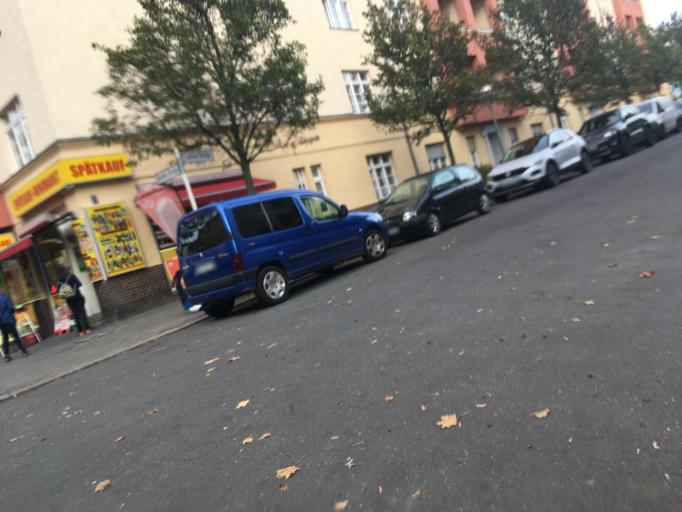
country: DE
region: Berlin
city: Gesundbrunnen
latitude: 52.5533
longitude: 13.3920
